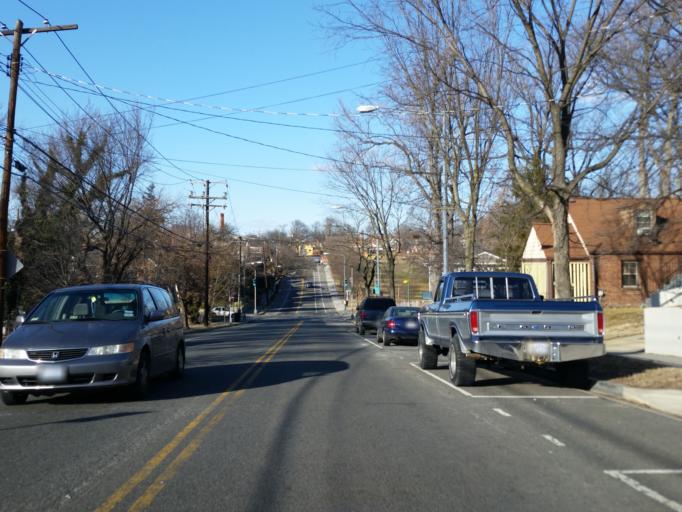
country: US
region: Maryland
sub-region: Prince George's County
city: Mount Rainier
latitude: 38.9246
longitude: -76.9790
